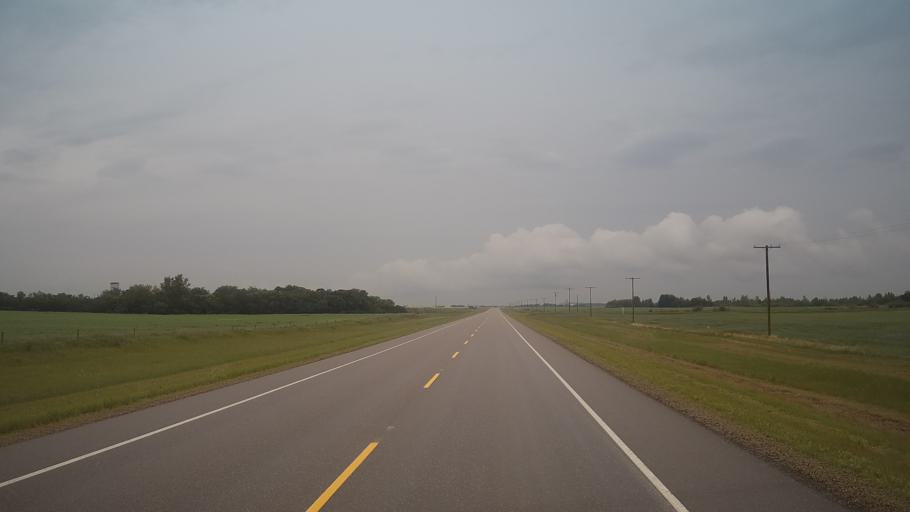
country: CA
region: Saskatchewan
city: Wilkie
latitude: 52.3157
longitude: -108.6972
